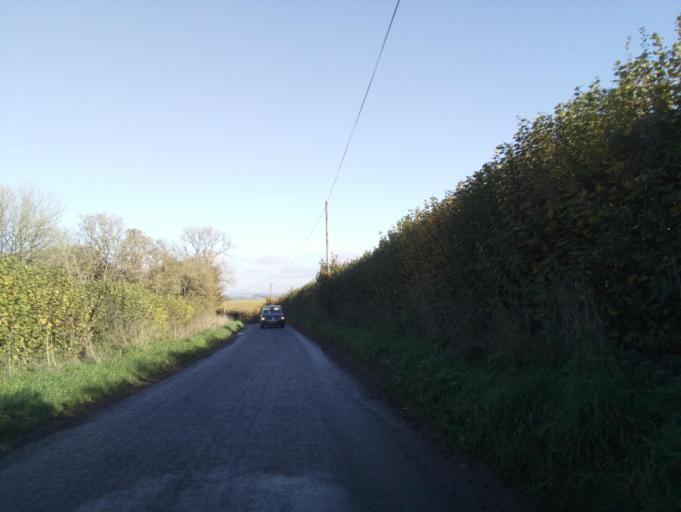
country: GB
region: England
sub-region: Somerset
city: Milborne Port
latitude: 51.0214
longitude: -2.4990
